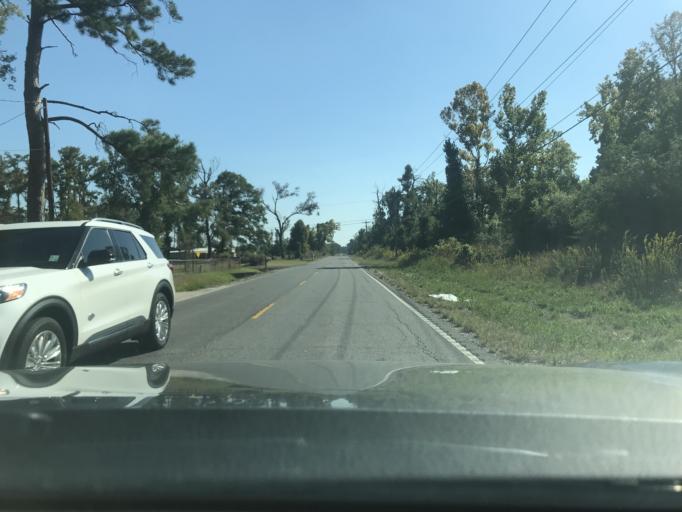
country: US
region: Louisiana
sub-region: Calcasieu Parish
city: Moss Bluff
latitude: 30.3186
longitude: -93.2583
